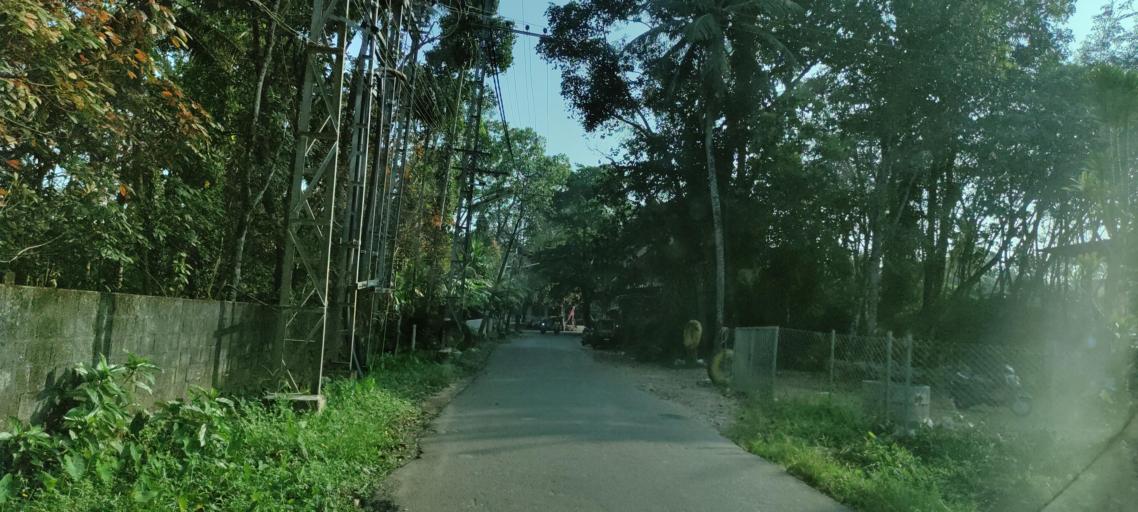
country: IN
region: Kerala
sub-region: Pattanamtitta
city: Adur
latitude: 9.1512
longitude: 76.7535
